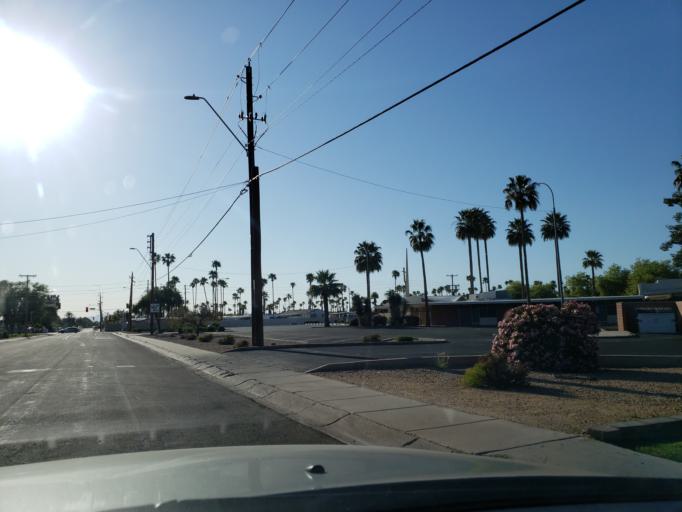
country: US
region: Arizona
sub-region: Maricopa County
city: Glendale
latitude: 33.5422
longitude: -112.1671
